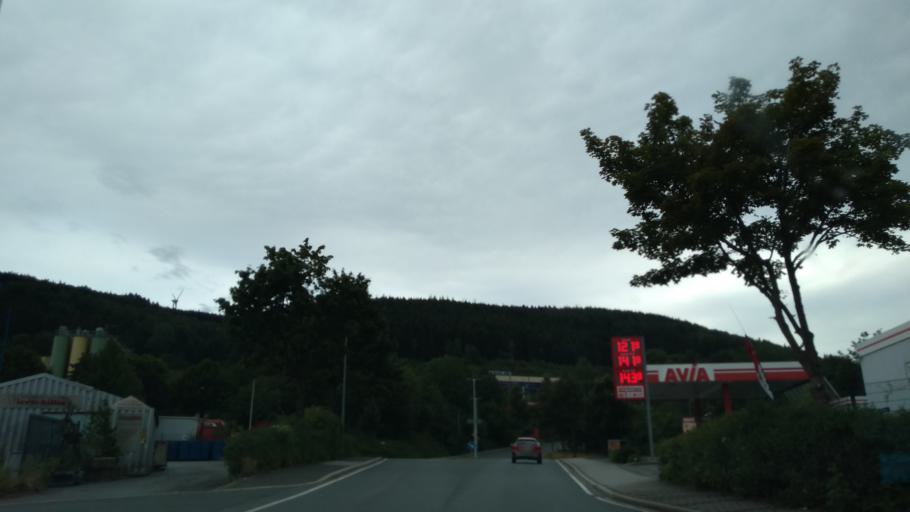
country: DE
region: North Rhine-Westphalia
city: Plettenberg
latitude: 51.1974
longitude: 7.8378
